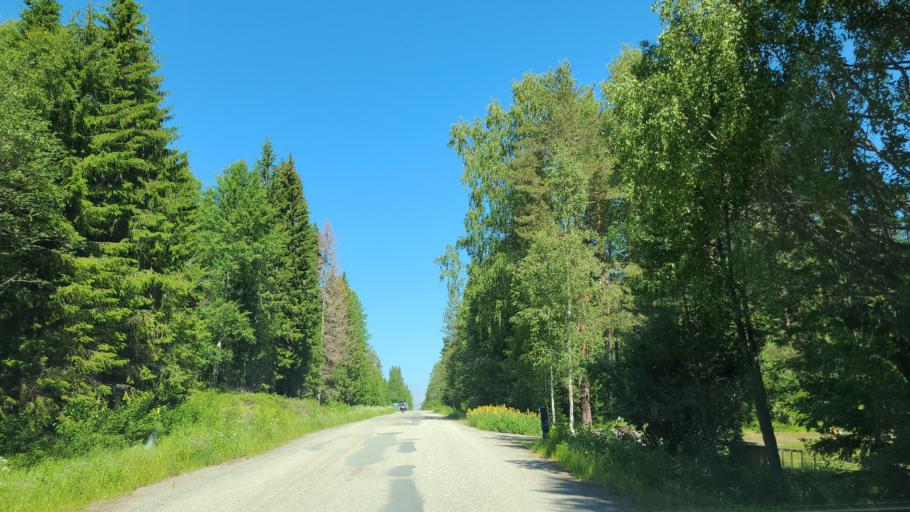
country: SE
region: Vaesternorrland
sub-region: OErnskoeldsviks Kommun
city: Husum
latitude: 63.4159
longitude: 19.2207
